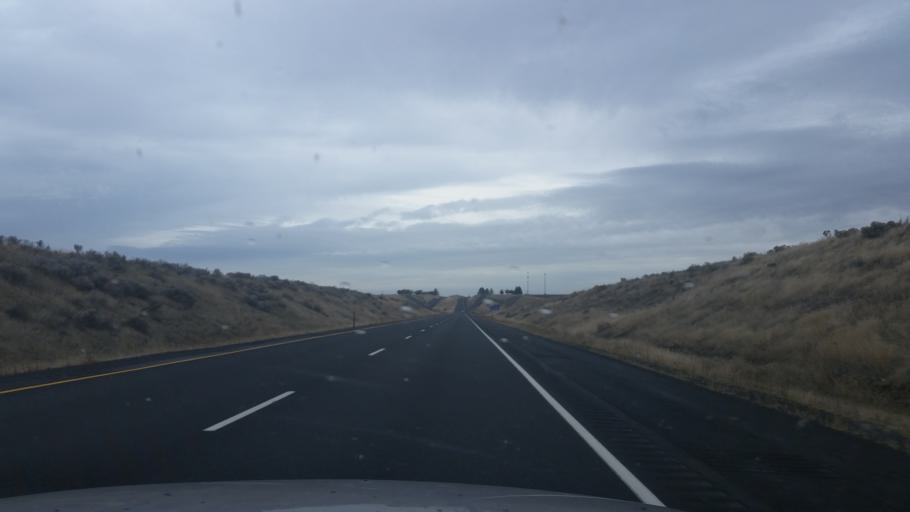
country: US
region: Washington
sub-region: Grant County
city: Warden
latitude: 47.0863
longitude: -118.8229
